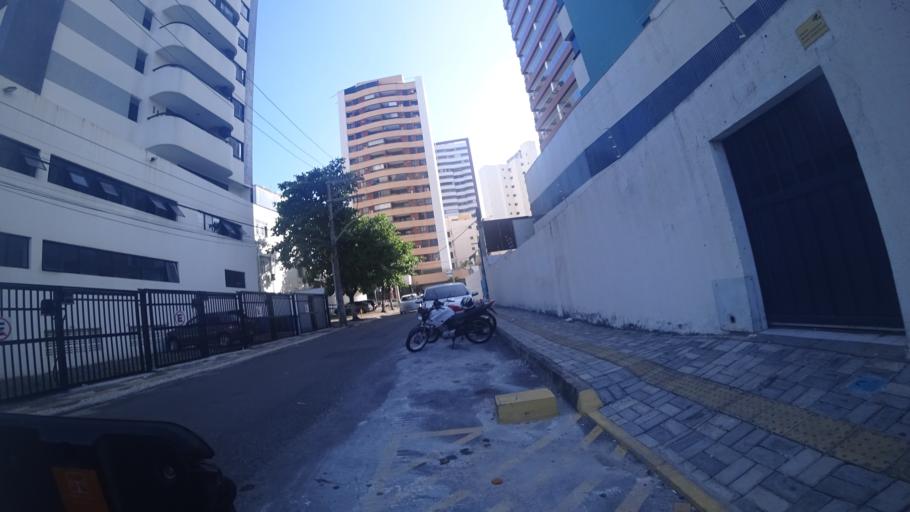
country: BR
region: Bahia
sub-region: Salvador
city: Salvador
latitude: -12.9963
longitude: -38.4516
